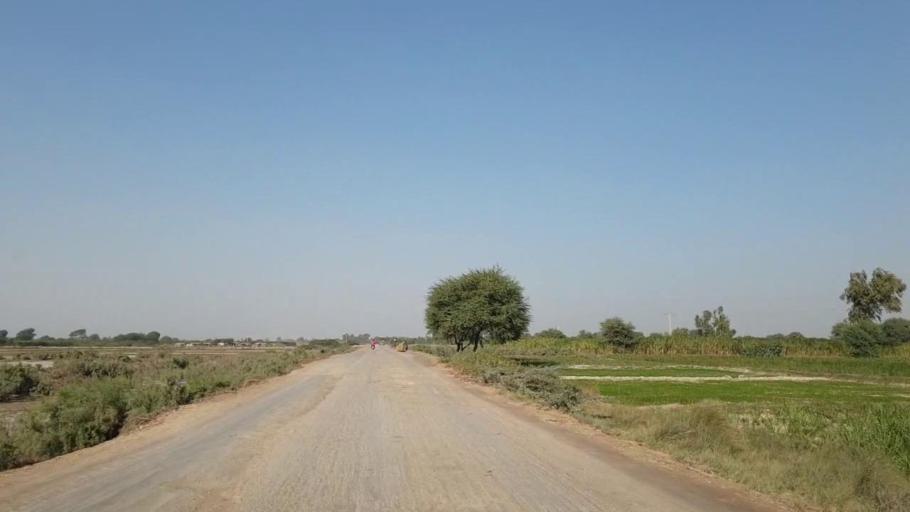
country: PK
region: Sindh
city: Digri
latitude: 25.0409
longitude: 69.1047
